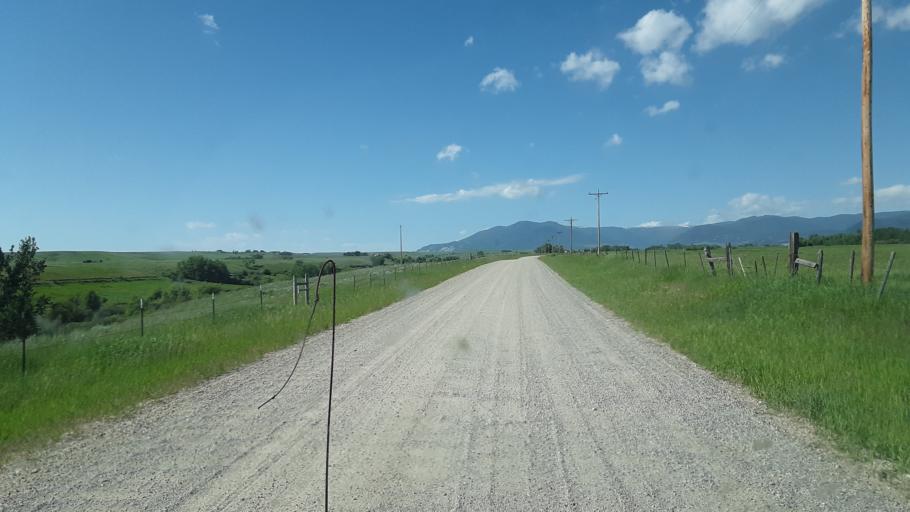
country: US
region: Montana
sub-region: Carbon County
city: Red Lodge
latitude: 45.2846
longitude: -109.1894
